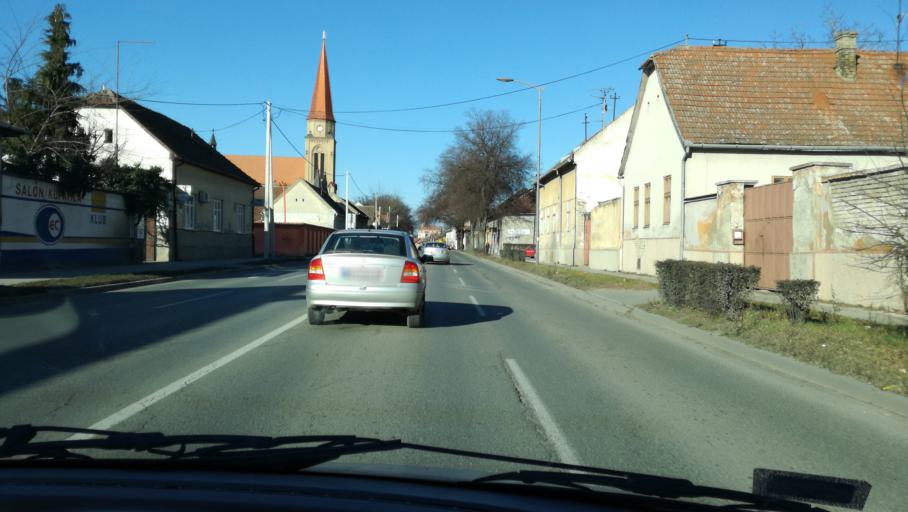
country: RS
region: Autonomna Pokrajina Vojvodina
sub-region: Severnobacki Okrug
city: Subotica
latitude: 46.0880
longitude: 19.6677
